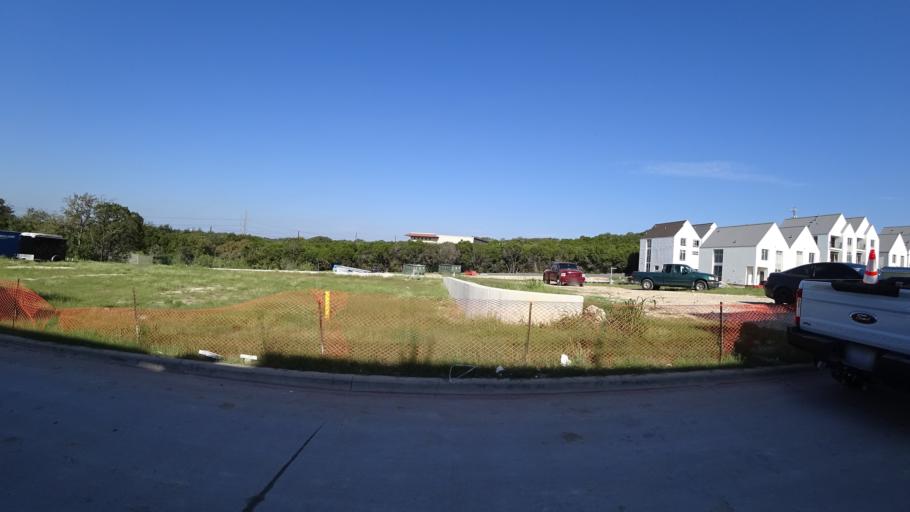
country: US
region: Texas
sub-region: Travis County
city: Rollingwood
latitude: 30.2601
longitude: -97.8117
